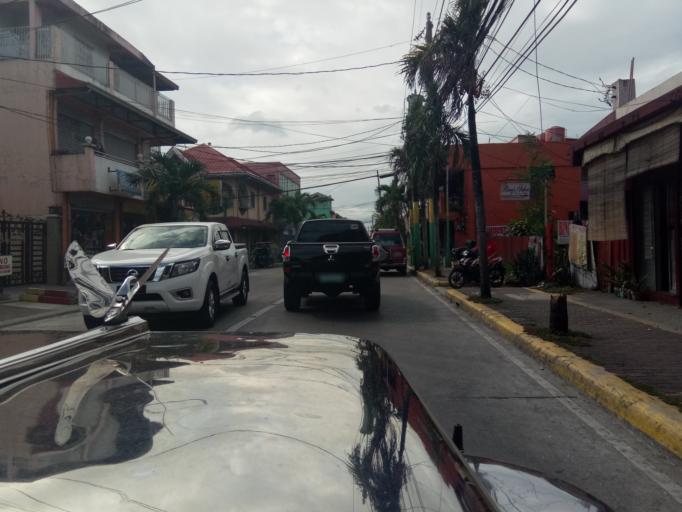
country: PH
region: Calabarzon
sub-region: Province of Cavite
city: Dasmarinas
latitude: 14.3205
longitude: 120.9400
